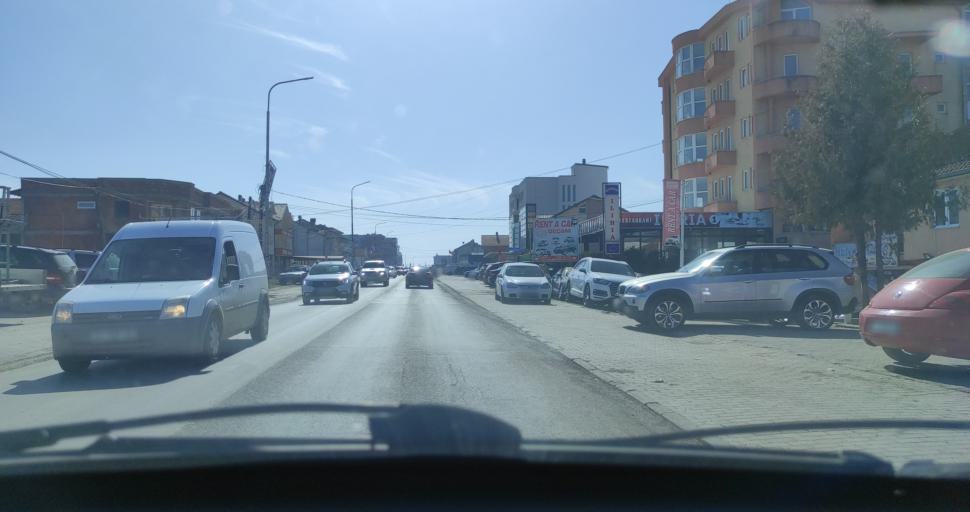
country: XK
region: Gjakova
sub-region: Komuna e Decanit
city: Decan
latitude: 42.5479
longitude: 20.2904
